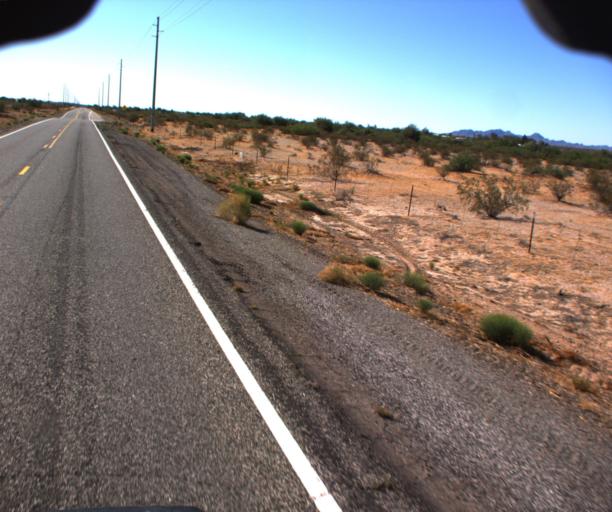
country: US
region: Arizona
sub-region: La Paz County
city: Cienega Springs
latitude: 33.9647
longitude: -114.0359
